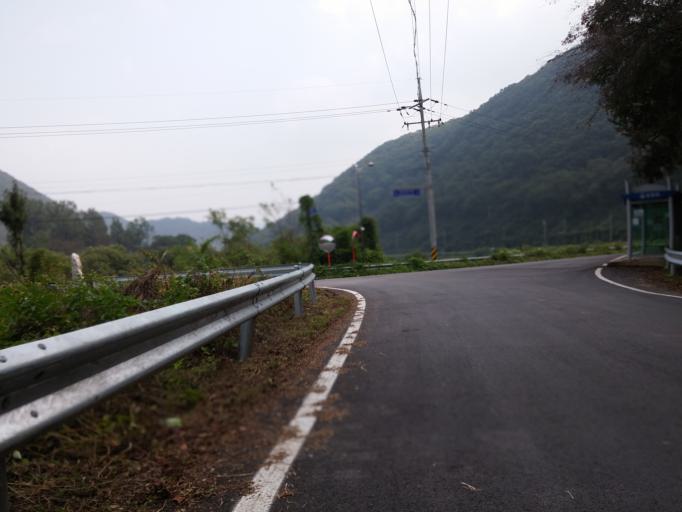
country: KR
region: Chungcheongbuk-do
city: Yong-dong
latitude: 36.3993
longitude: 127.8027
